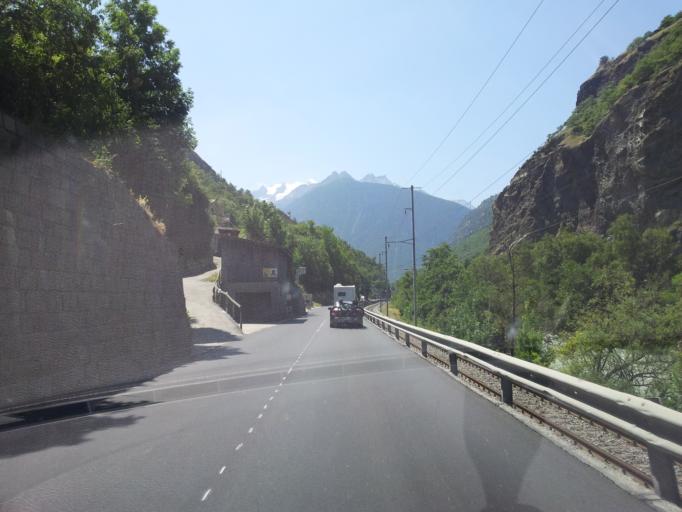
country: CH
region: Valais
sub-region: Visp District
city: Visp
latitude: 46.2741
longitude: 7.8820
